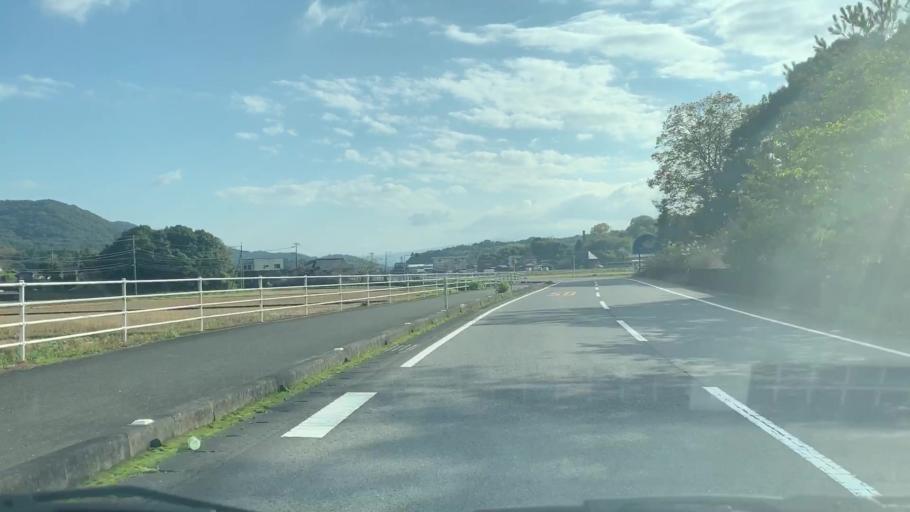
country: JP
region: Saga Prefecture
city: Takeocho-takeo
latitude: 33.1614
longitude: 130.0614
